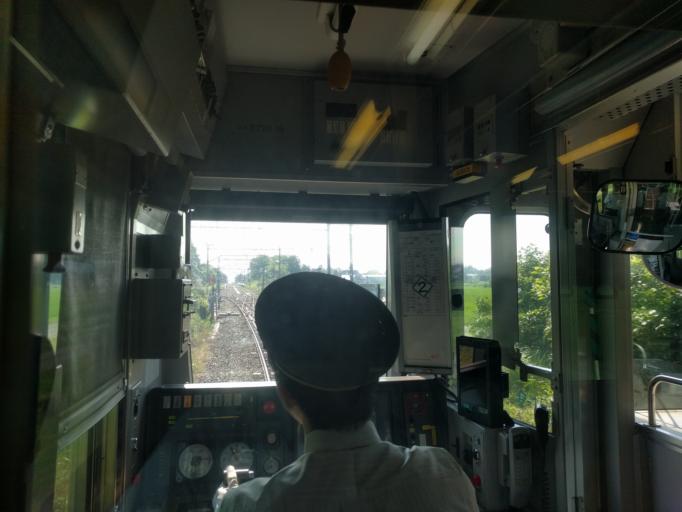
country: JP
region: Fukushima
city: Inawashiro
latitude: 37.5532
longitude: 140.0509
